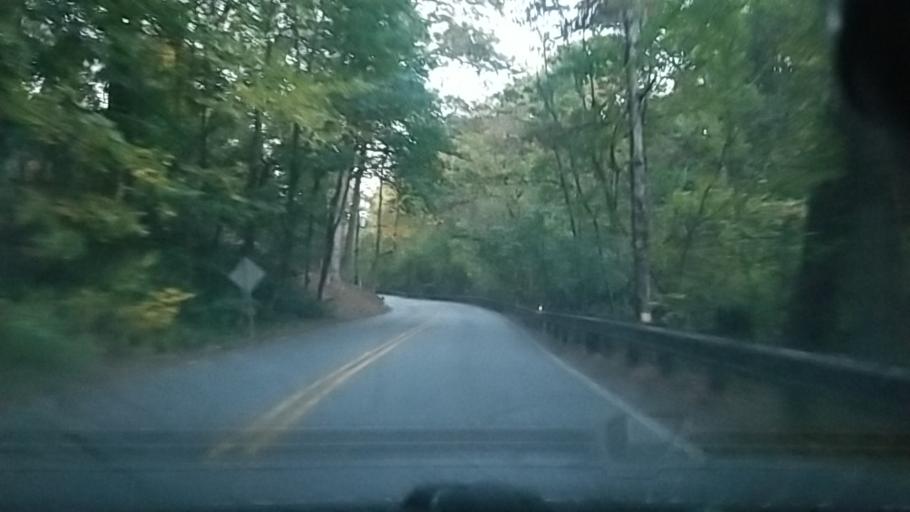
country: US
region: Maryland
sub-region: Montgomery County
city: Takoma Park
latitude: 38.9798
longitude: -76.9953
